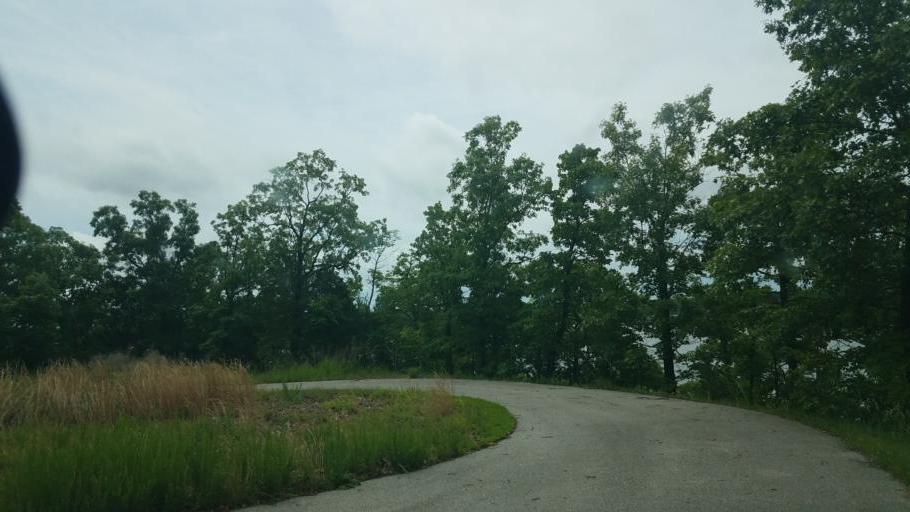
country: US
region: Missouri
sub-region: Camden County
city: Osage Beach
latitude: 38.1545
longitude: -92.6894
